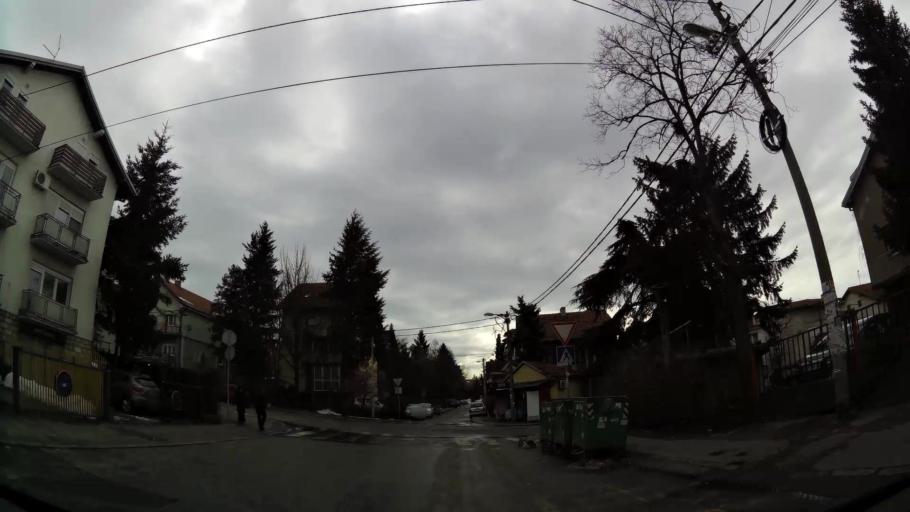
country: RS
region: Central Serbia
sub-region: Belgrade
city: Cukarica
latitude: 44.7508
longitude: 20.4071
